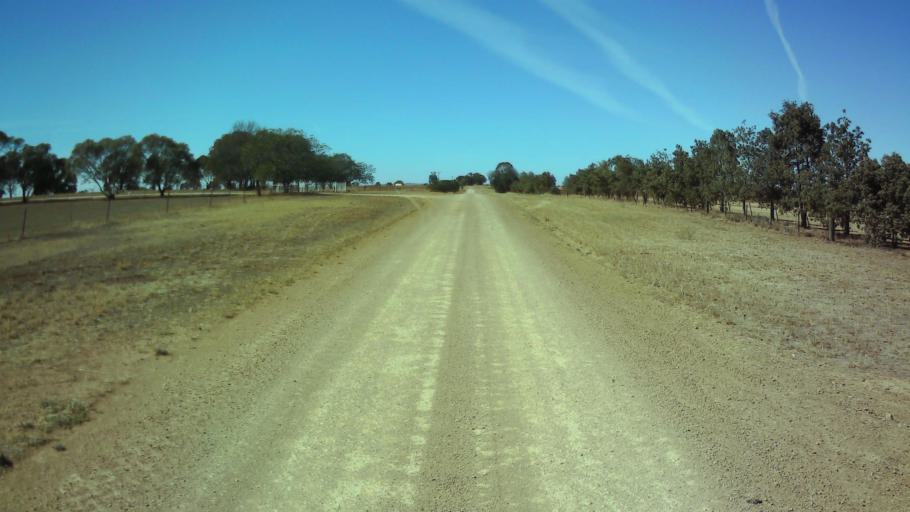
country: AU
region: New South Wales
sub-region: Weddin
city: Grenfell
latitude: -34.0549
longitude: 148.1720
